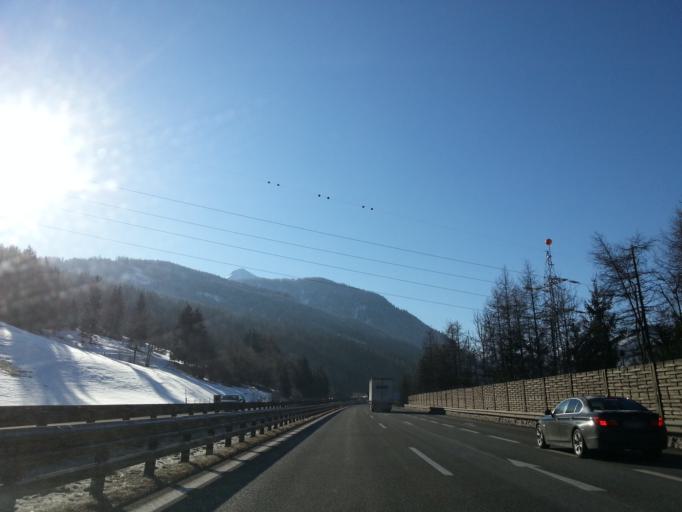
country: AT
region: Salzburg
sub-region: Politischer Bezirk Sankt Johann im Pongau
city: Flachau
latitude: 47.3642
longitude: 13.3964
